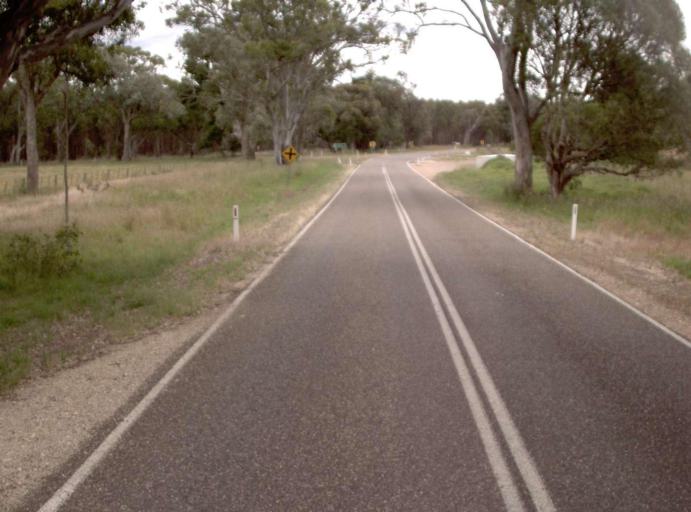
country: AU
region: Victoria
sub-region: East Gippsland
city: Bairnsdale
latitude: -37.7947
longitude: 147.3306
